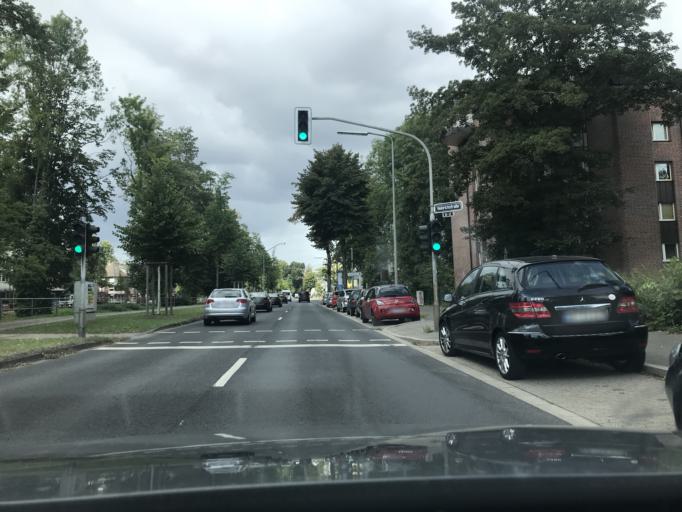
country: DE
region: North Rhine-Westphalia
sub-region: Regierungsbezirk Dusseldorf
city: Dusseldorf
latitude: 51.2442
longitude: 6.8128
